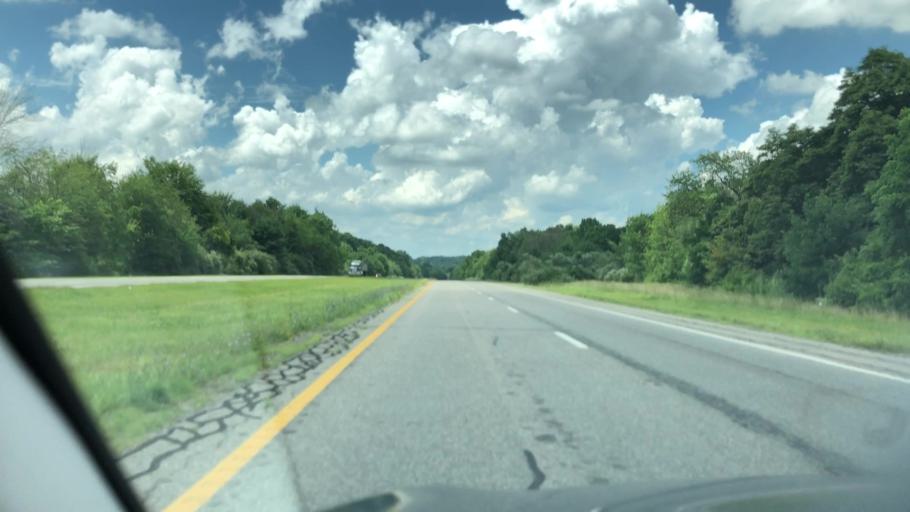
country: US
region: Ohio
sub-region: Summit County
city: Clinton
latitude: 40.8960
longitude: -81.6328
